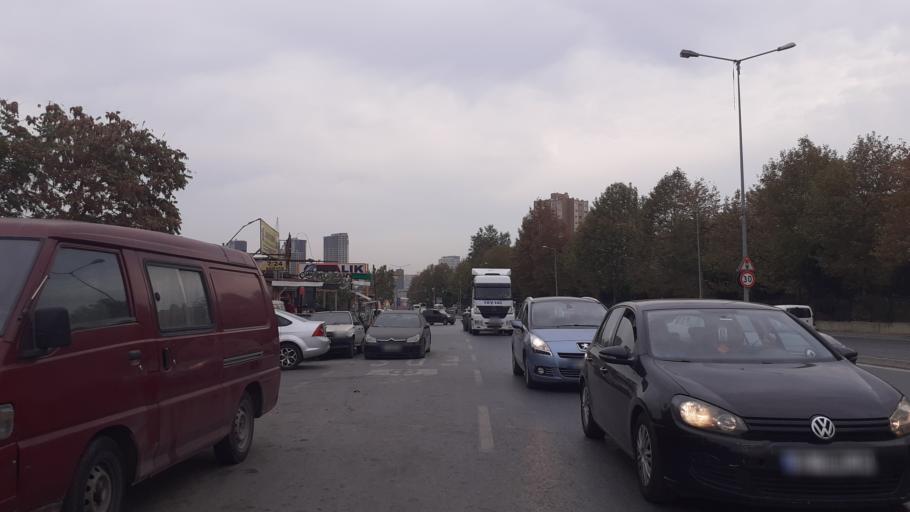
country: TR
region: Istanbul
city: Mahmutbey
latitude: 41.0486
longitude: 28.7985
